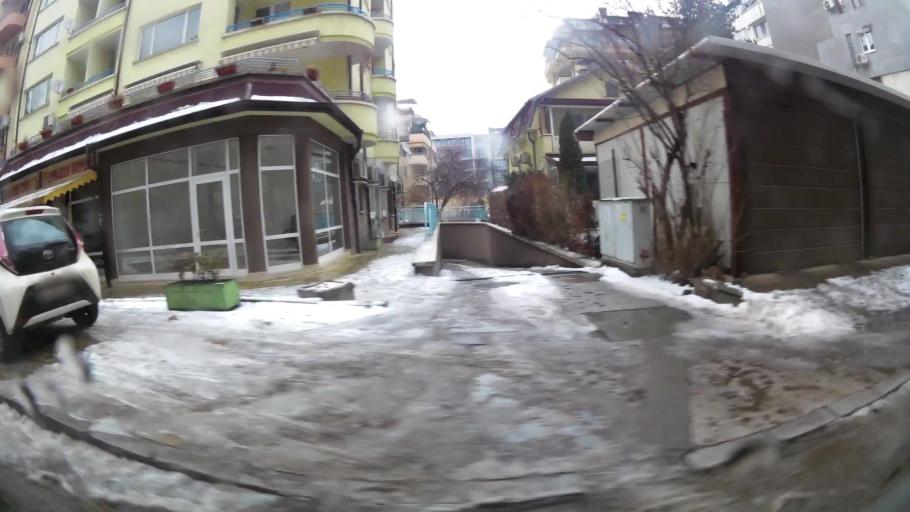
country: BG
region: Sofia-Capital
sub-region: Stolichna Obshtina
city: Sofia
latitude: 42.6689
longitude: 23.2843
